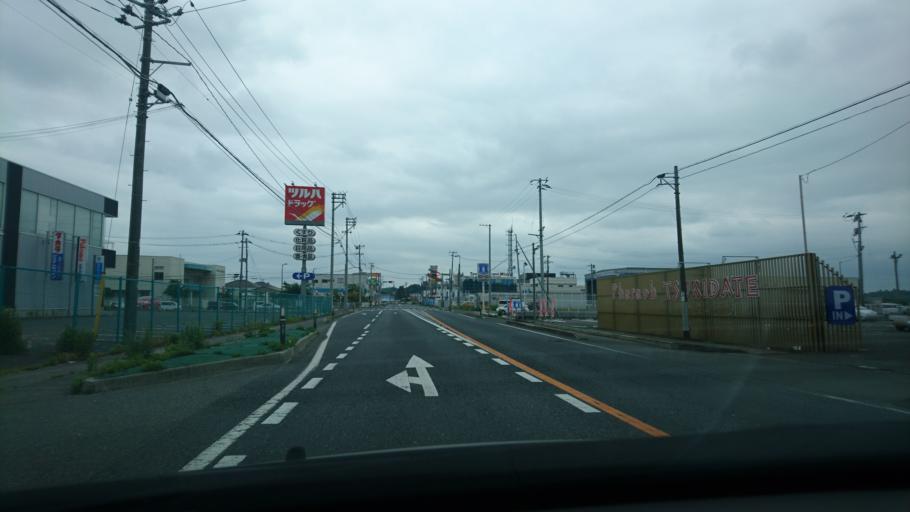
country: JP
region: Miyagi
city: Furukawa
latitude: 38.7473
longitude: 141.0145
